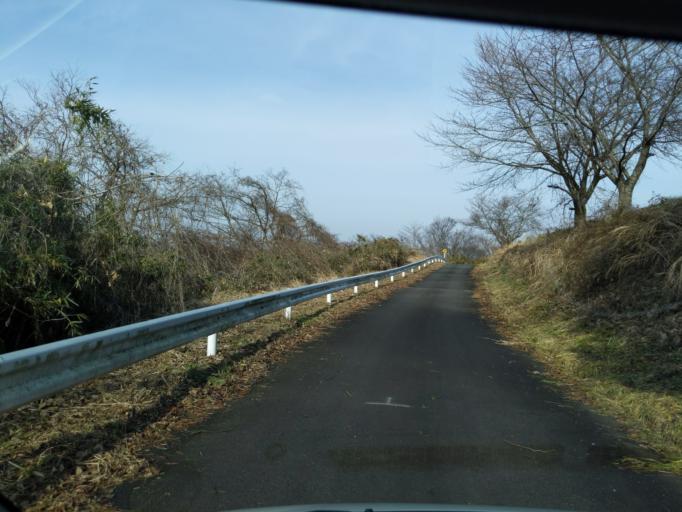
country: JP
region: Miyagi
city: Wakuya
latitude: 38.7017
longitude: 141.1503
